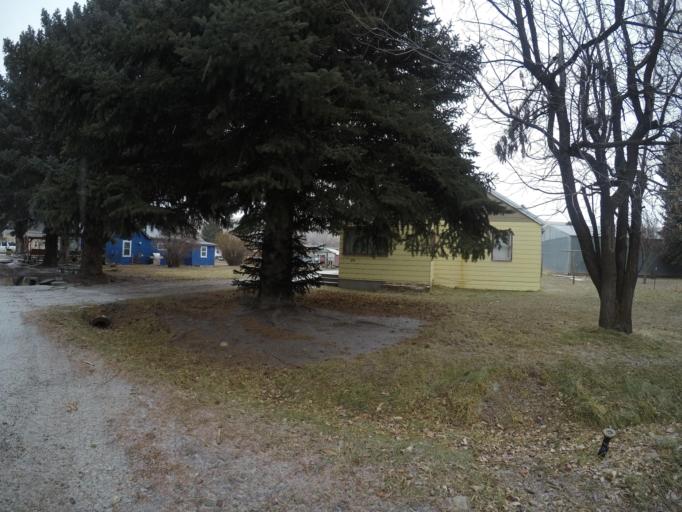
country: US
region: Montana
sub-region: Stillwater County
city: Absarokee
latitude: 45.5151
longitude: -109.4458
